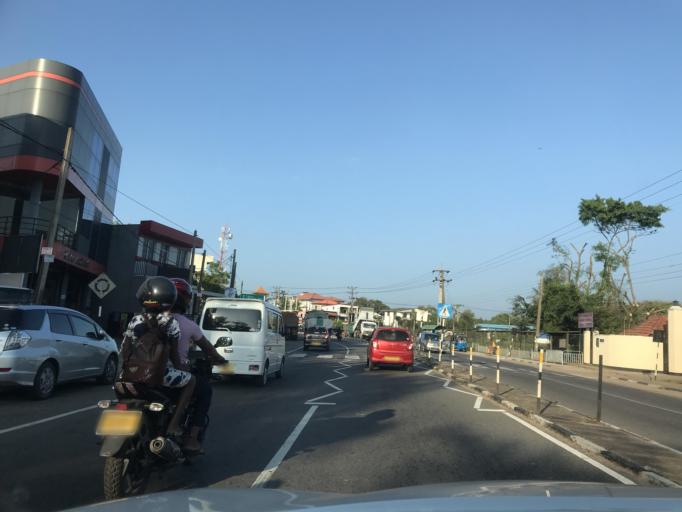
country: LK
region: Western
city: Ja Ela
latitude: 7.1003
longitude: 79.9097
